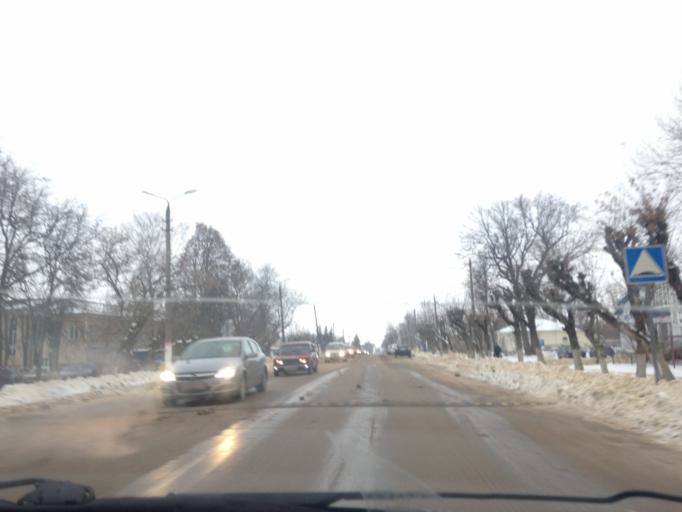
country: RU
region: Tula
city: Shchekino
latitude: 54.0006
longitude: 37.5101
